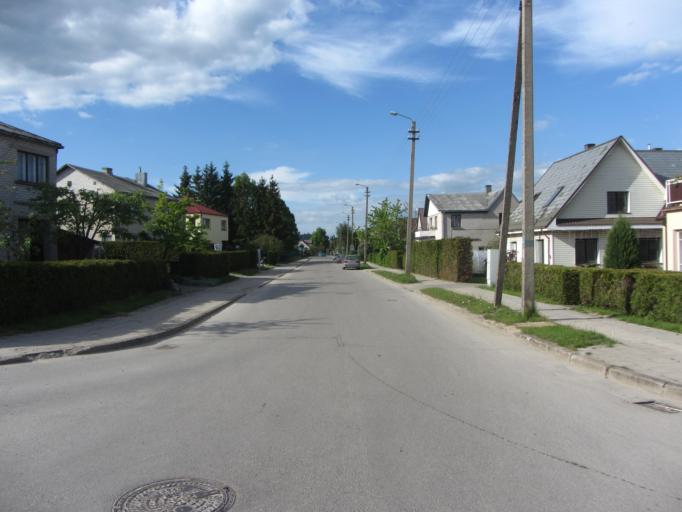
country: LT
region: Utenos apskritis
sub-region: Utena
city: Utena
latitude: 55.4914
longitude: 25.6013
